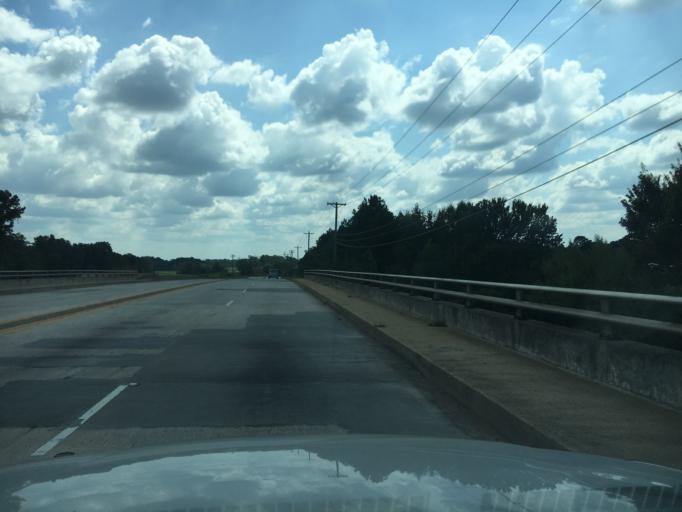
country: US
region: South Carolina
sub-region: Greenwood County
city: Greenwood
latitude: 34.1783
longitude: -82.1839
